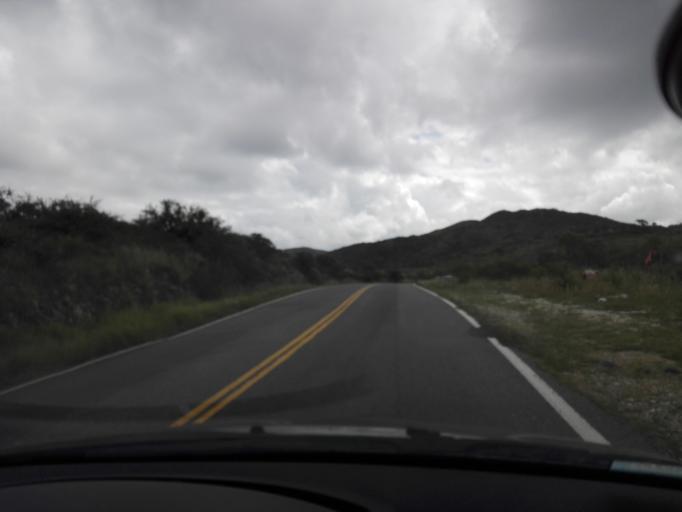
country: AR
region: Cordoba
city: Alta Gracia
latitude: -31.5930
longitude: -64.5239
